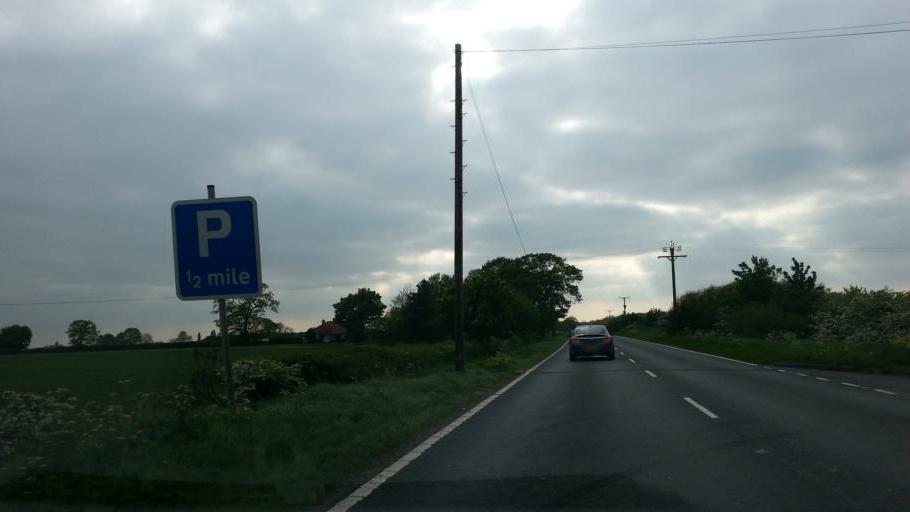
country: GB
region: England
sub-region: Lincolnshire
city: Long Bennington
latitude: 53.0696
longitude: -0.6558
